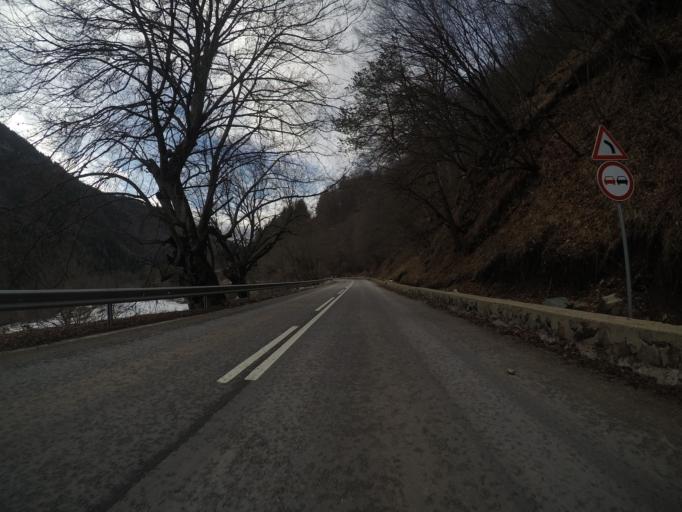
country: BG
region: Kyustendil
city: Sapareva Banya
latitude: 42.1142
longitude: 23.3122
